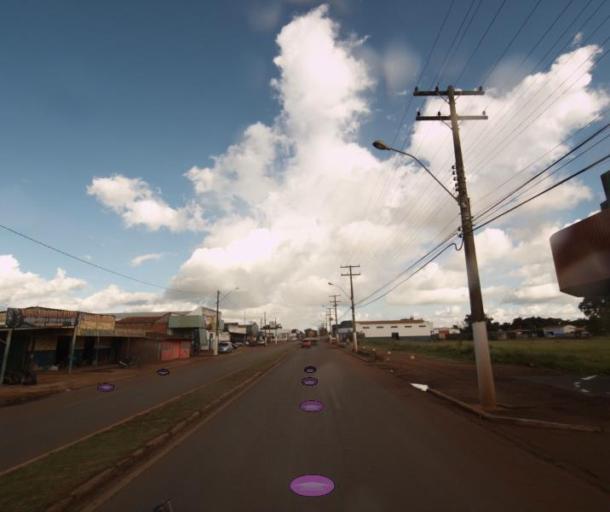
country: BR
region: Goias
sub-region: Itaberai
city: Itaberai
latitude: -16.0407
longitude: -49.7921
